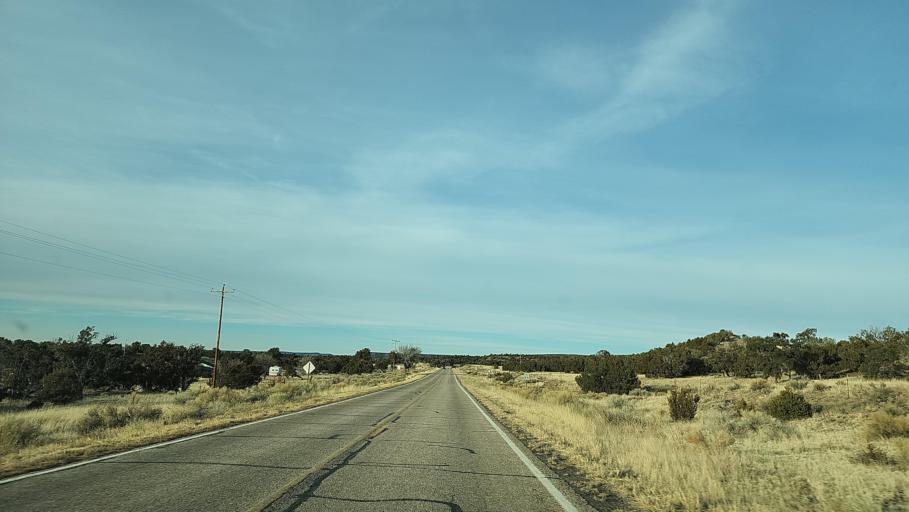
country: US
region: New Mexico
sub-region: McKinley County
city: Black Rock
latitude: 34.4200
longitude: -108.4299
